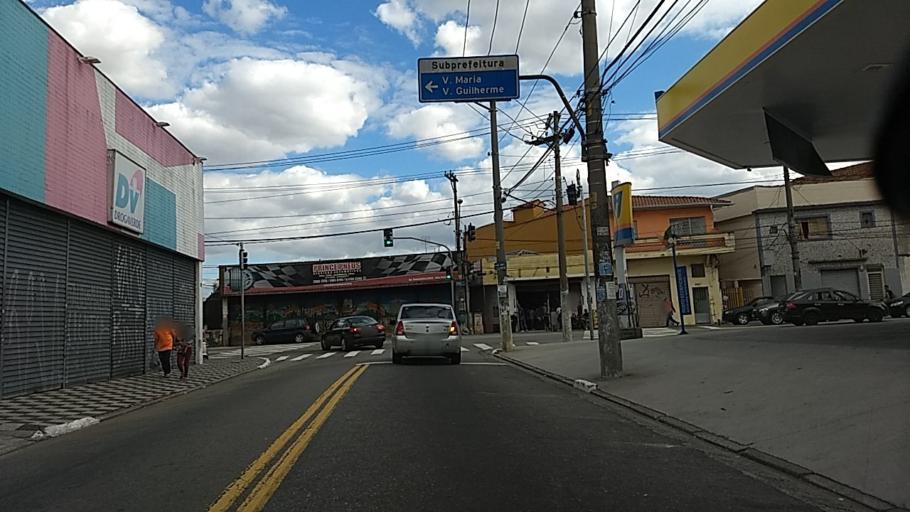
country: BR
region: Sao Paulo
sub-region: Sao Paulo
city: Sao Paulo
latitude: -23.4984
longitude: -46.5950
